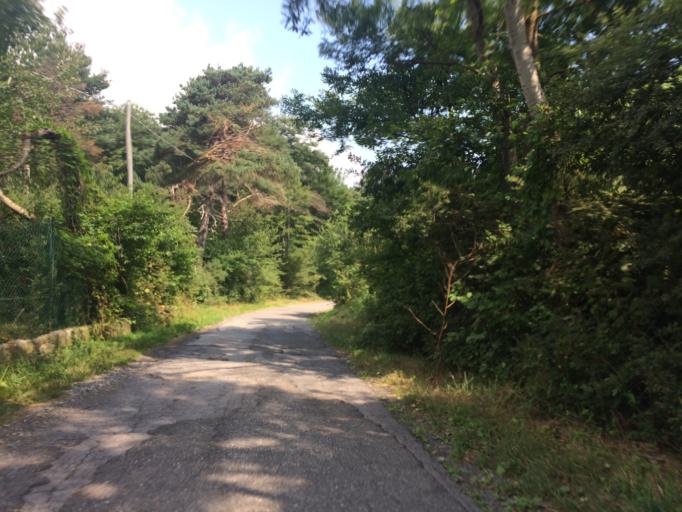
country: IT
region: Liguria
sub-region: Provincia di Savona
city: Piana Crixia
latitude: 44.4674
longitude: 8.3488
